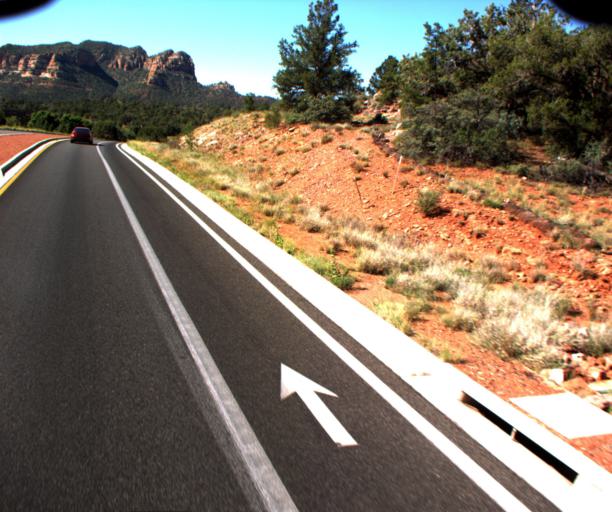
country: US
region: Arizona
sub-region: Coconino County
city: Sedona
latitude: 34.8291
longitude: -111.7780
